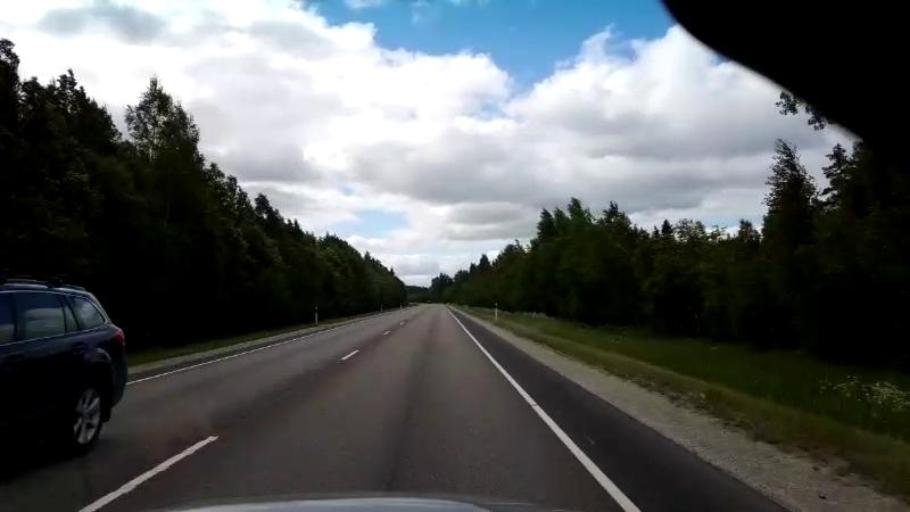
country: EE
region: Paernumaa
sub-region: Halinga vald
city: Parnu-Jaagupi
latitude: 58.7091
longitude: 24.4240
